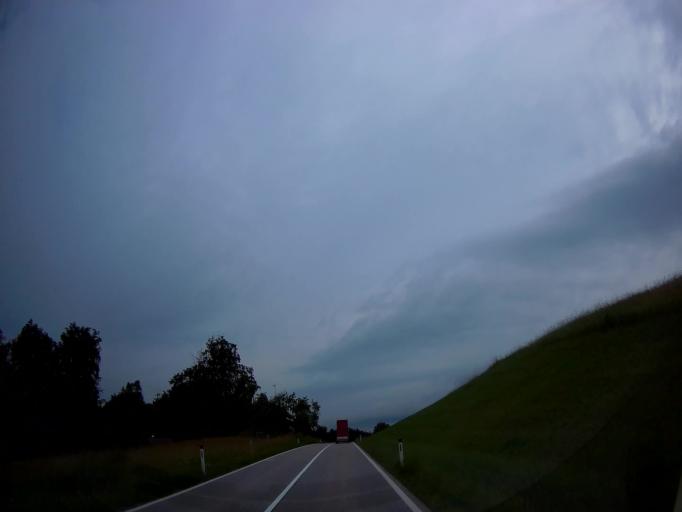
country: AT
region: Salzburg
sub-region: Politischer Bezirk Salzburg-Umgebung
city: Mattsee
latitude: 48.0306
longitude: 13.1423
